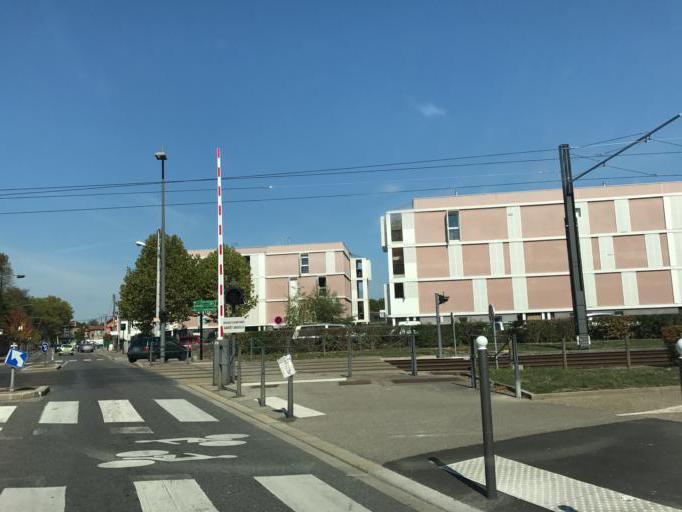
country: FR
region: Rhone-Alpes
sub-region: Departement du Rhone
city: Meyzieu
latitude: 45.7712
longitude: 5.0009
